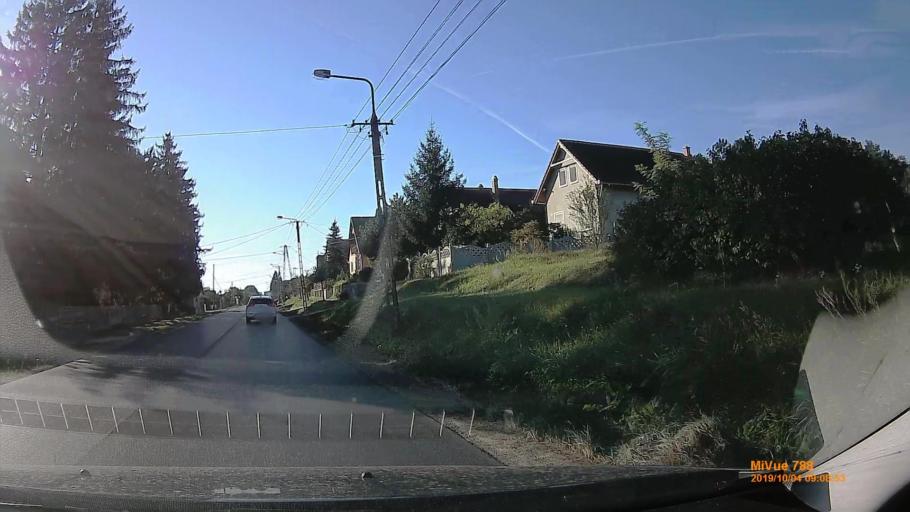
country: HU
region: Somogy
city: Karad
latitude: 46.6676
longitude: 17.7787
